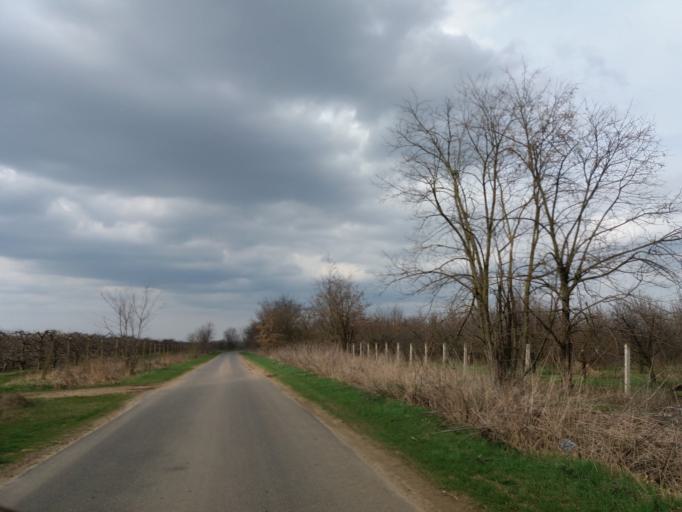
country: HU
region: Szabolcs-Szatmar-Bereg
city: Nyirtass
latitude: 48.0939
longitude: 22.0306
